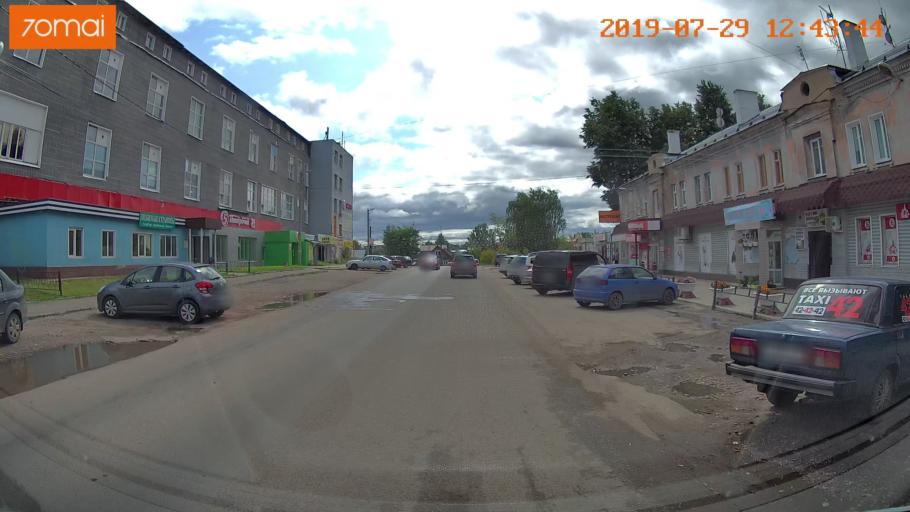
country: RU
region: Ivanovo
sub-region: Gorod Ivanovo
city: Ivanovo
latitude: 57.0006
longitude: 40.9305
